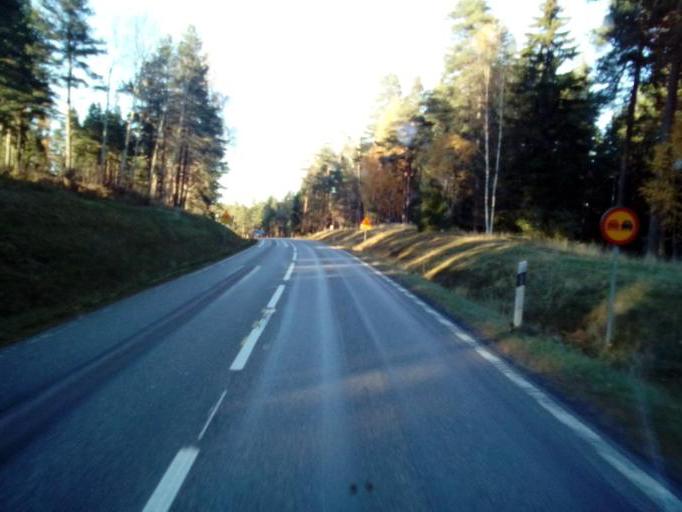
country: SE
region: OErebro
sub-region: Hallsbergs Kommun
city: Palsboda
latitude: 58.8999
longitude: 15.4352
